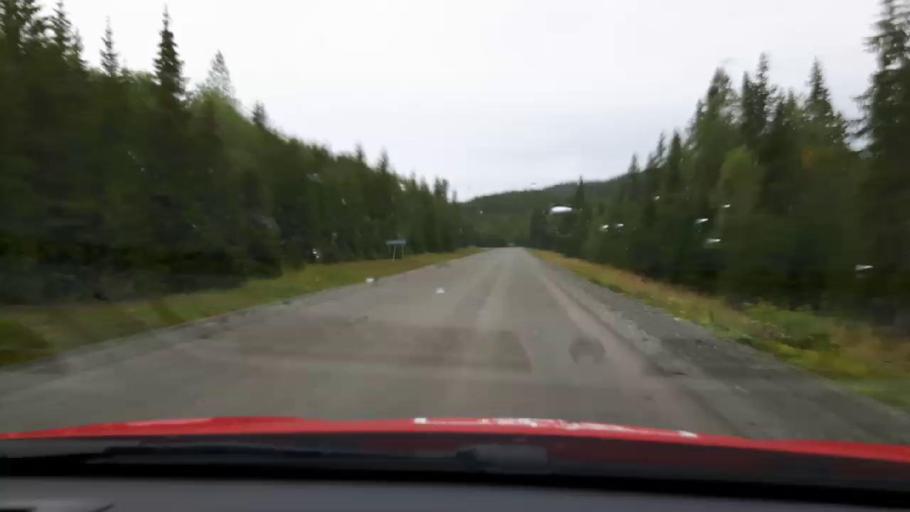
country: SE
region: Jaemtland
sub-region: Are Kommun
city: Are
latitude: 63.4257
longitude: 12.7402
